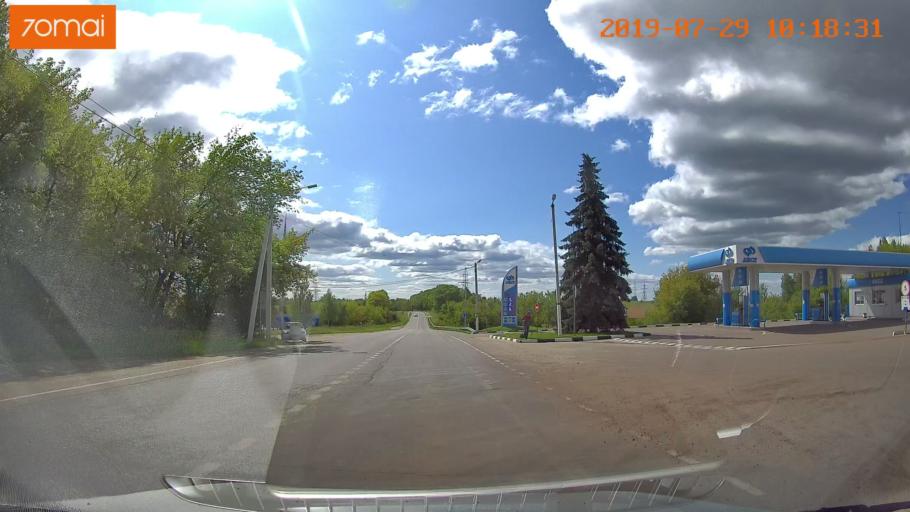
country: RU
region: Moskovskaya
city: Voskresensk
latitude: 55.3036
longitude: 38.6604
